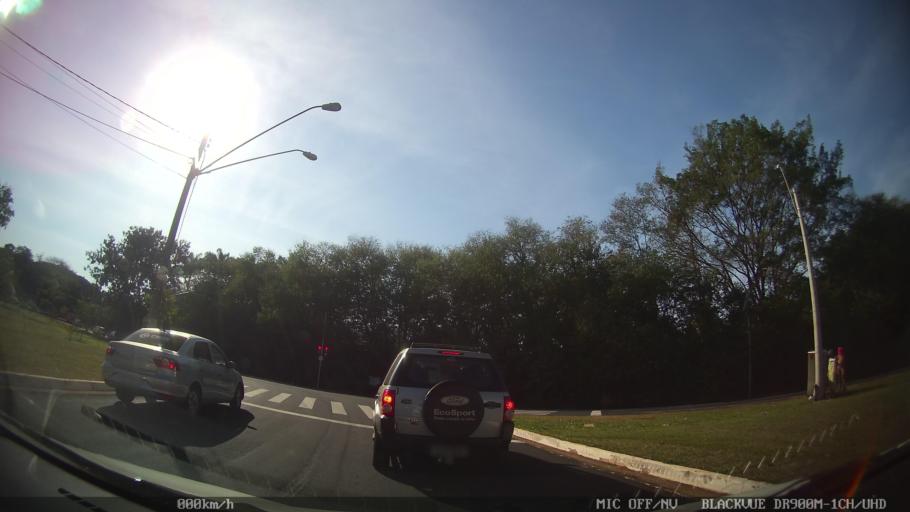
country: BR
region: Sao Paulo
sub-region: Ribeirao Preto
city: Ribeirao Preto
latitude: -21.2191
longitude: -47.8157
